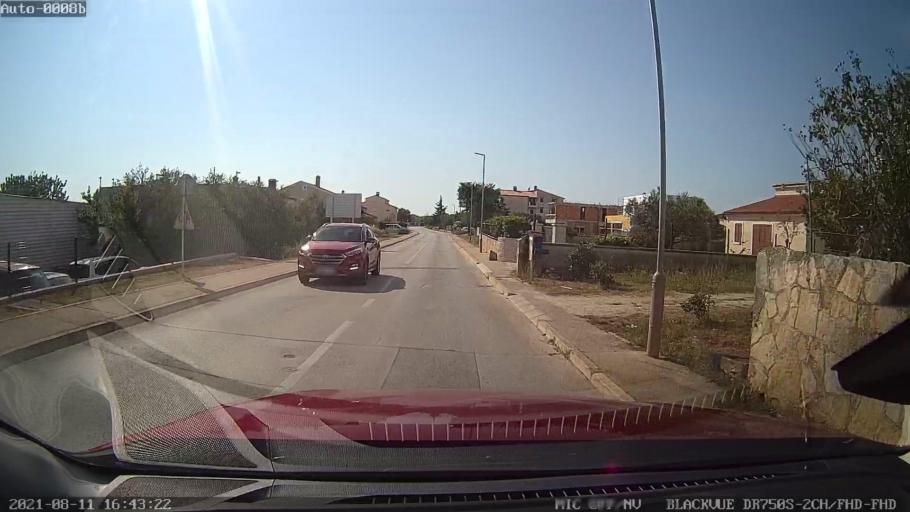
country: HR
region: Istarska
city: Vodnjan
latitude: 44.9543
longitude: 13.8525
